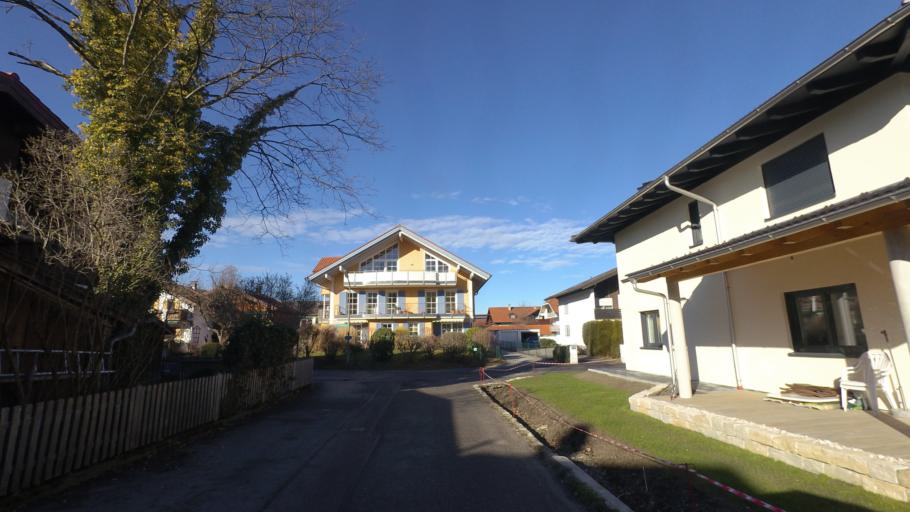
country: DE
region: Bavaria
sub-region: Upper Bavaria
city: Bernau am Chiemsee
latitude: 47.8231
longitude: 12.3867
